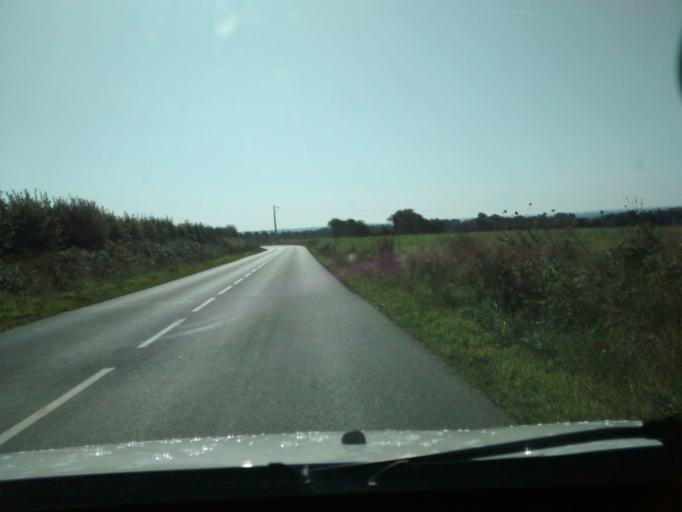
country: FR
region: Brittany
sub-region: Departement des Cotes-d'Armor
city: Penvenan
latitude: 48.7825
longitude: -3.3231
